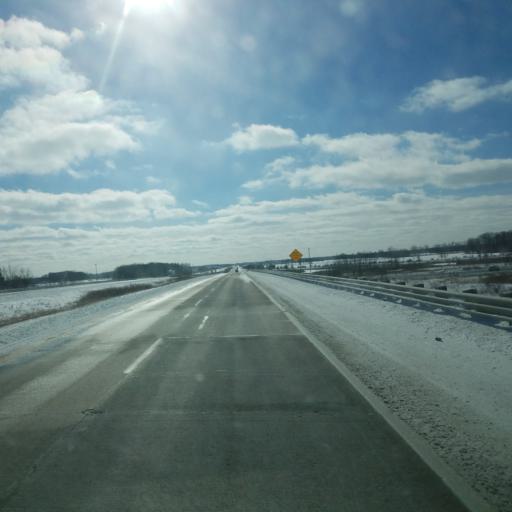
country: US
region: Michigan
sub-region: Clinton County
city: Saint Johns
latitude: 43.0037
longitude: -84.5192
